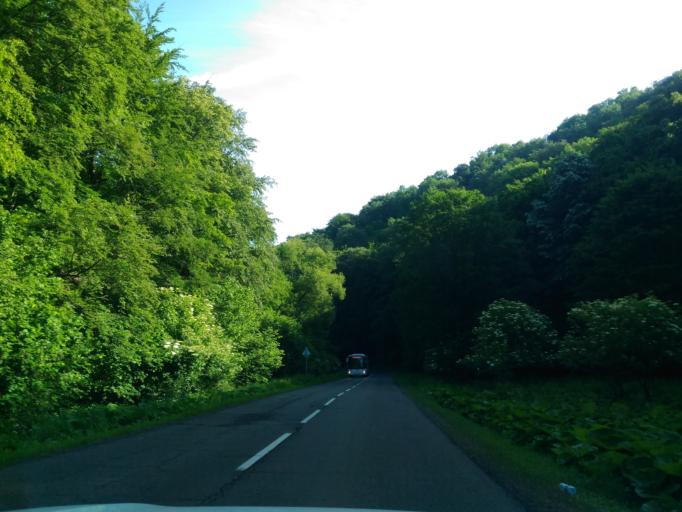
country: HU
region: Baranya
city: Komlo
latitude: 46.2065
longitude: 18.3001
